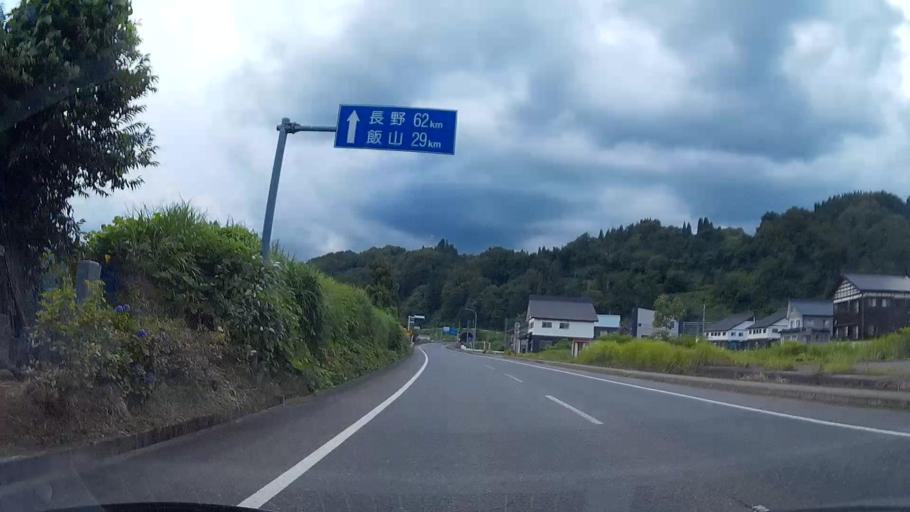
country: JP
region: Nagano
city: Iiyama
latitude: 36.9888
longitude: 138.5644
